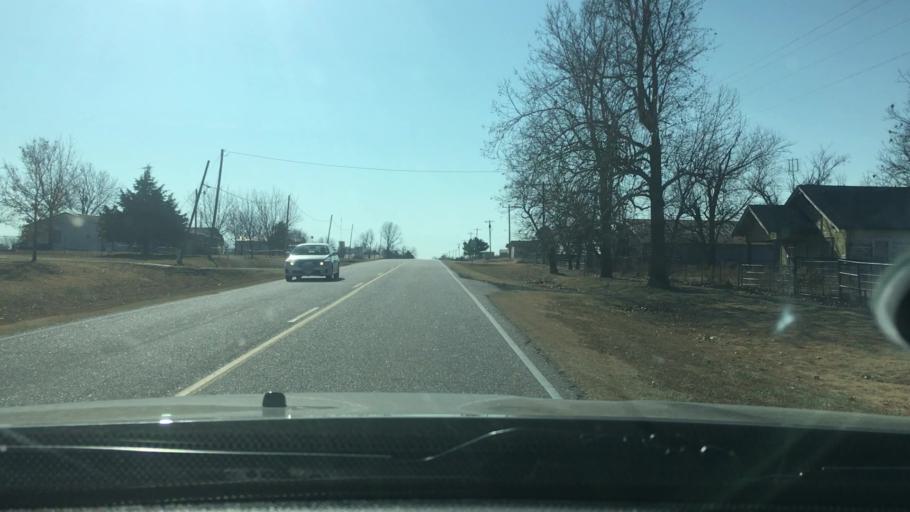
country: US
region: Oklahoma
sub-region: Garvin County
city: Stratford
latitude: 34.8044
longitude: -96.9676
